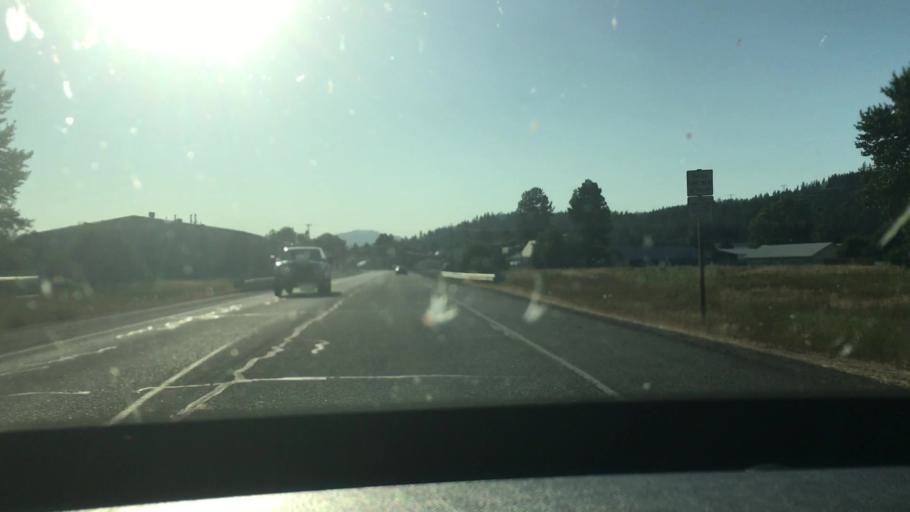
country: US
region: Washington
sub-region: Kittitas County
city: Cle Elum
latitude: 47.1911
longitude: -120.9130
